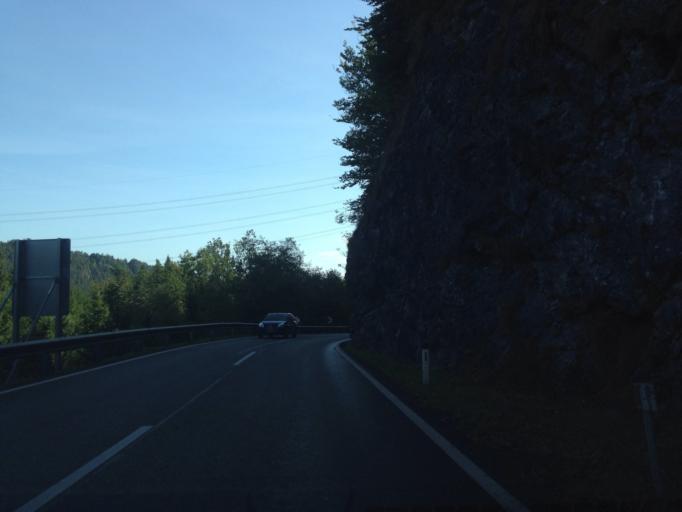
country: AT
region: Tyrol
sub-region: Politischer Bezirk Reutte
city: Musau
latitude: 47.5496
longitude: 10.6635
